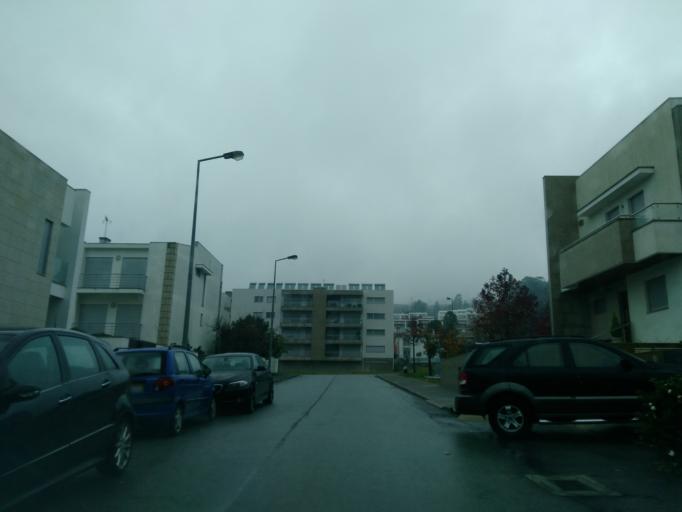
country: PT
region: Braga
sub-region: Braga
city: Adaufe
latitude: 41.5687
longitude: -8.3765
